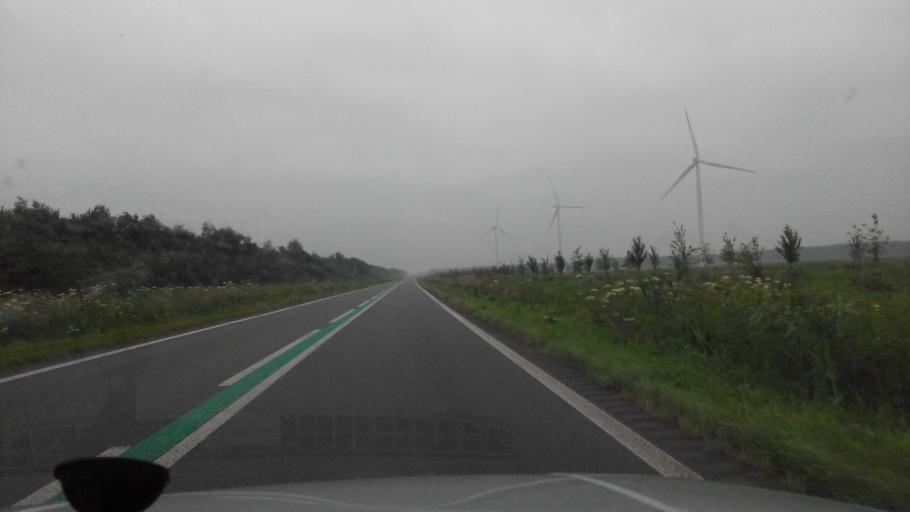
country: NL
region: Gelderland
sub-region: Gemeente Nijkerk
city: Nijkerk
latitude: 52.2967
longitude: 5.4546
